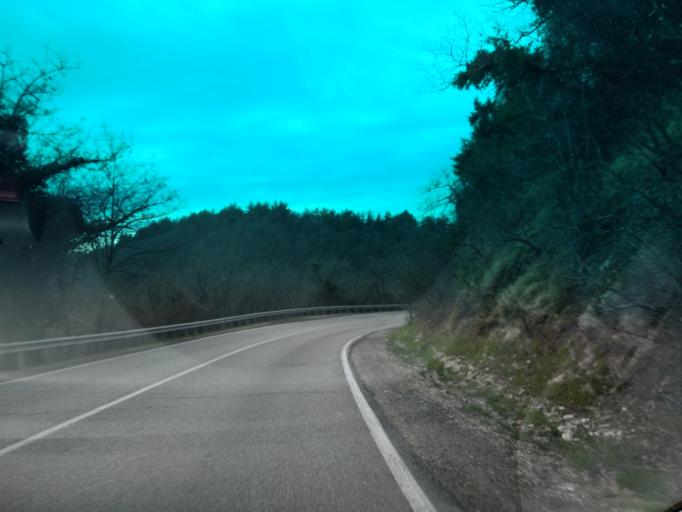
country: RU
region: Krasnodarskiy
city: Tuapse
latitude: 44.0897
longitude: 39.1195
